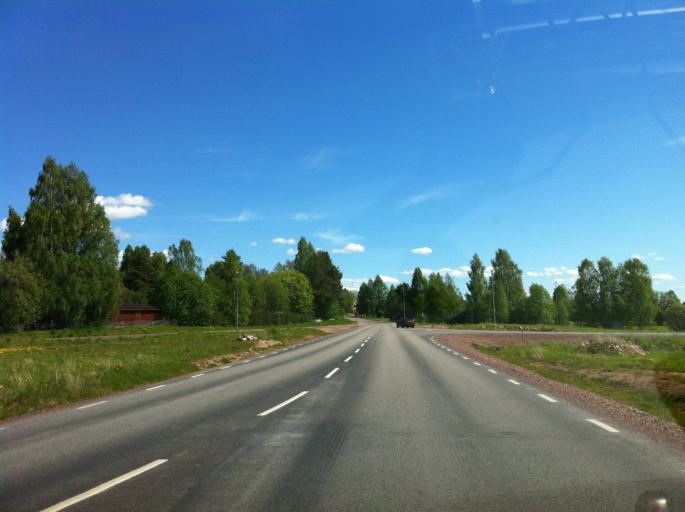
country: SE
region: Dalarna
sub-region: Mora Kommun
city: Mora
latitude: 61.0065
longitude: 14.6068
